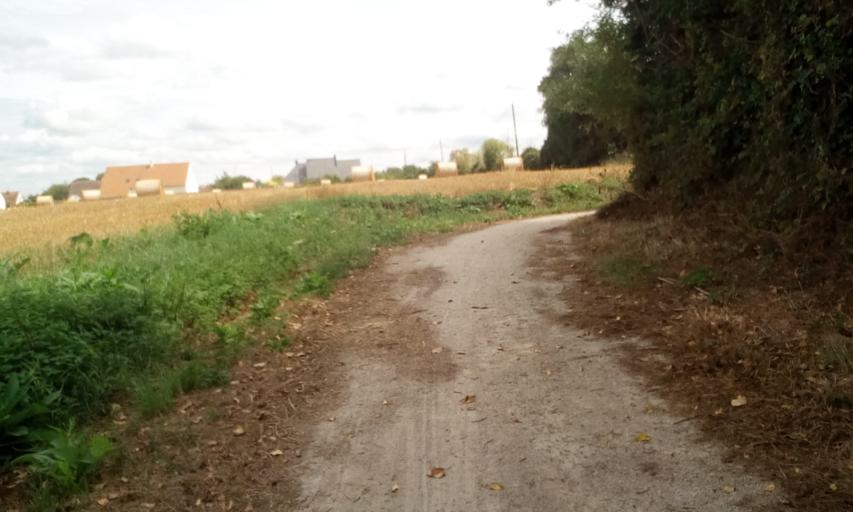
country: FR
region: Lower Normandy
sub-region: Departement du Calvados
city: Merville-Franceville-Plage
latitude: 49.2536
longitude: -0.1948
